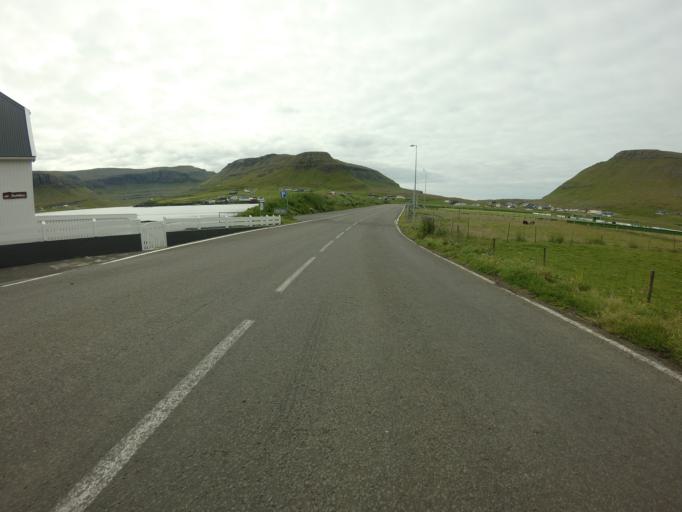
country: FO
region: Suduroy
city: Tvoroyri
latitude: 61.6030
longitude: -6.9509
